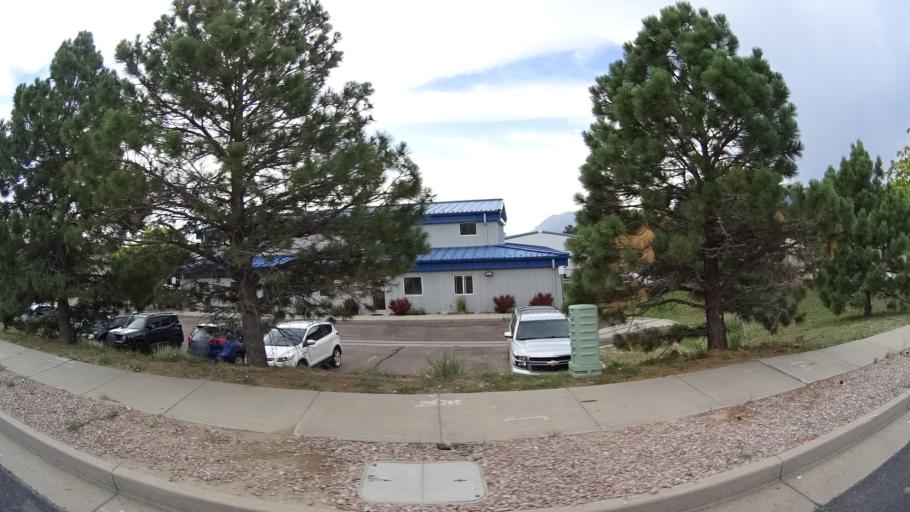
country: US
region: Colorado
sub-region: El Paso County
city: Colorado Springs
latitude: 38.9007
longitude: -104.8328
